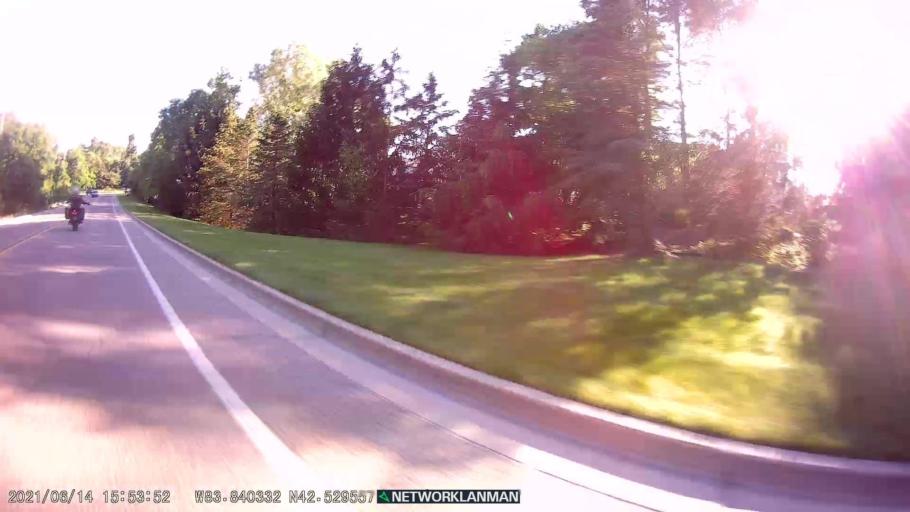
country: US
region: Michigan
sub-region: Livingston County
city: Brighton
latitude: 42.5293
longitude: -83.8403
